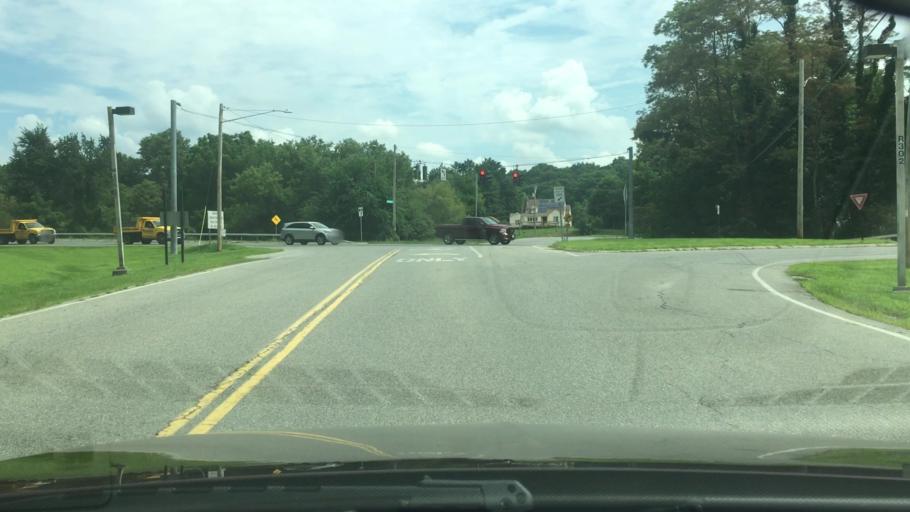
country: US
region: New York
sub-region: Dutchess County
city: Brinckerhoff
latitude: 41.5441
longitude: -73.8177
